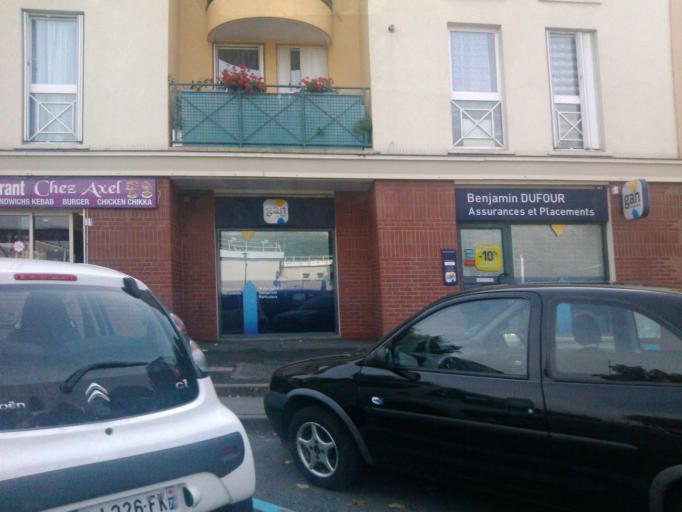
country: FR
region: Ile-de-France
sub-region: Departement des Yvelines
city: Plaisir
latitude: 48.8314
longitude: 1.9428
